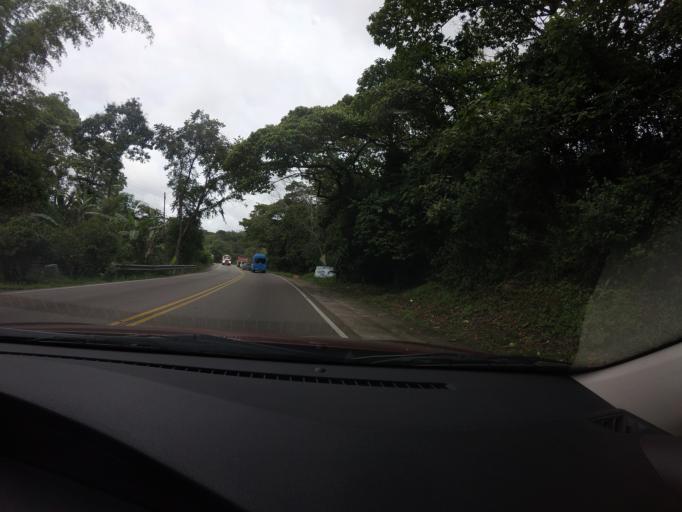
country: CO
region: Cundinamarca
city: Granada
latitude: 5.0587
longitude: -74.5786
